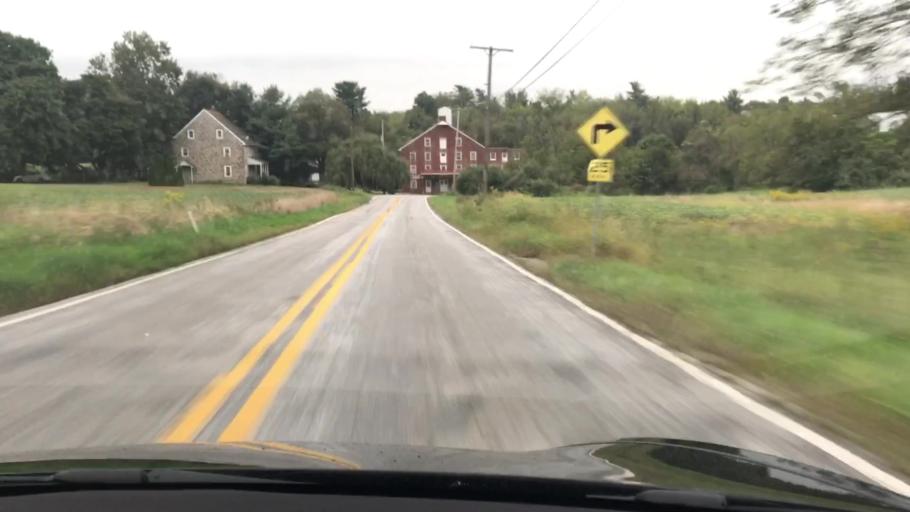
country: US
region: Pennsylvania
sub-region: York County
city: Weigelstown
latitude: 39.9421
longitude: -76.8609
